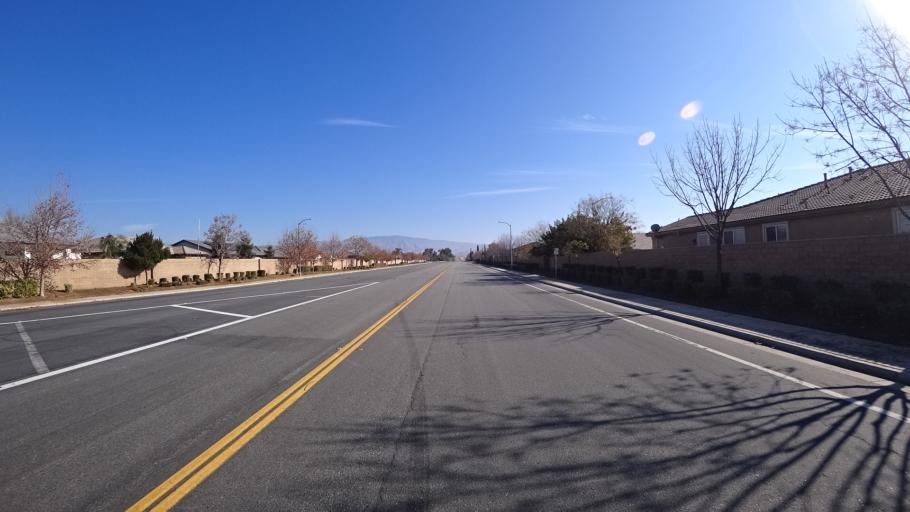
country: US
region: California
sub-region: Kern County
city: Oildale
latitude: 35.4125
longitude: -118.8910
